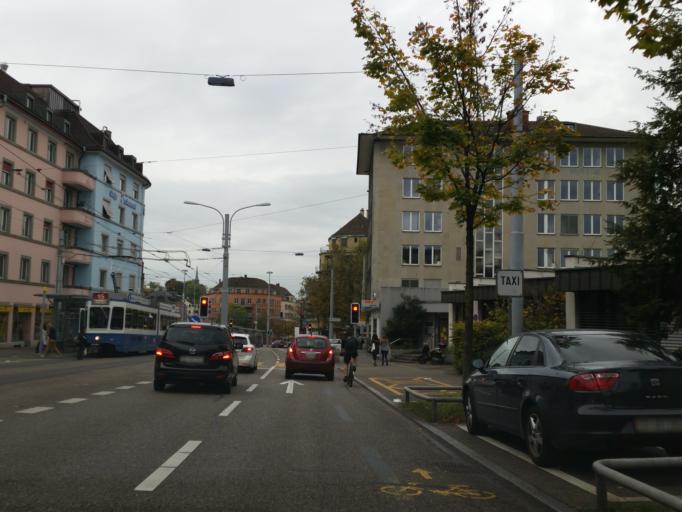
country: CH
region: Zurich
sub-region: Bezirk Zuerich
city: Zuerich (Kreis 6) / Unterstrass
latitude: 47.3928
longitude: 8.5380
